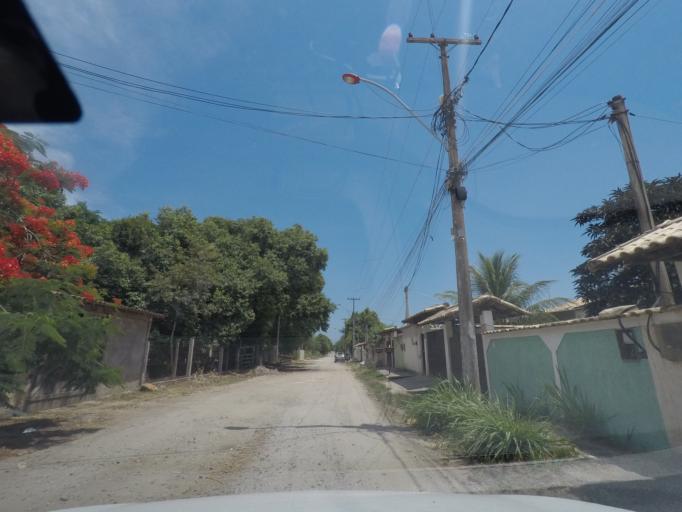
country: BR
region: Rio de Janeiro
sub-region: Niteroi
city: Niteroi
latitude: -22.9571
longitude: -42.9694
